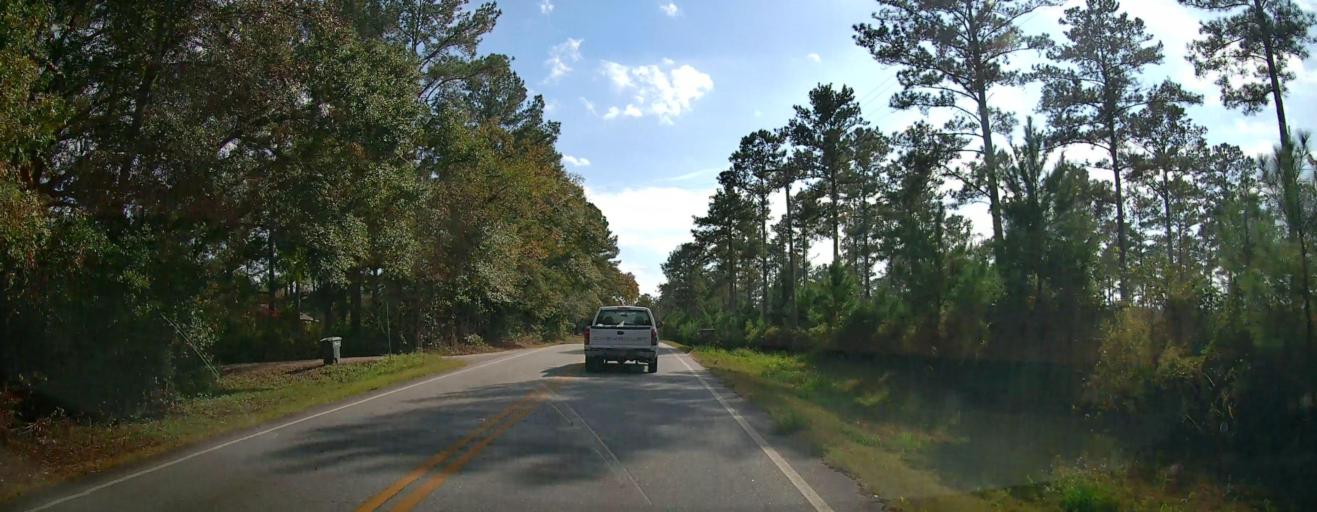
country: US
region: Georgia
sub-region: Thomas County
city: Thomasville
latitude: 30.9015
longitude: -84.0062
